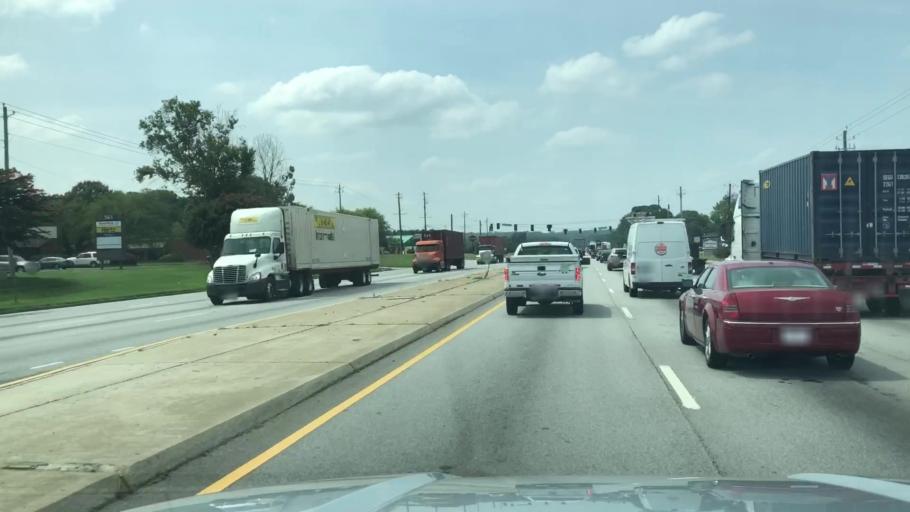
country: US
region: Georgia
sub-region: Cobb County
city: Austell
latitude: 33.7899
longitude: -84.6245
